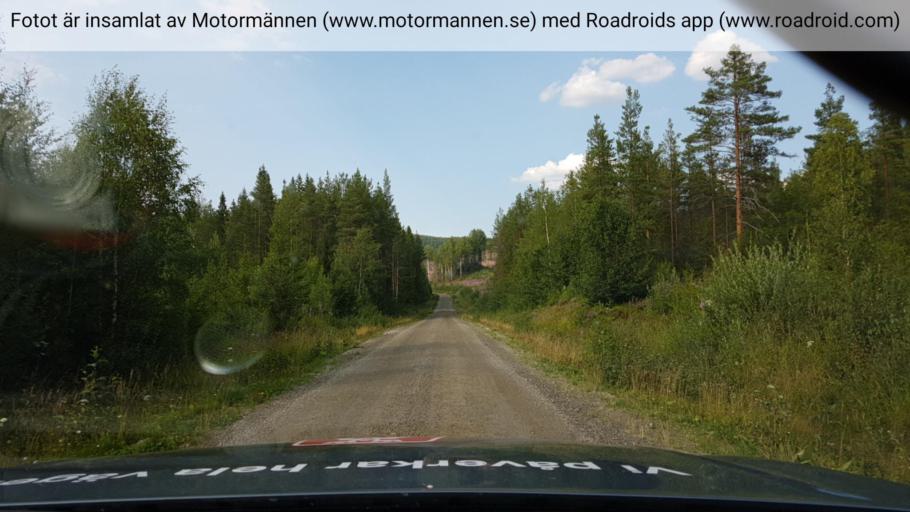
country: SE
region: Jaemtland
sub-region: Bergs Kommun
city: Hoverberg
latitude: 62.5251
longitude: 14.9144
